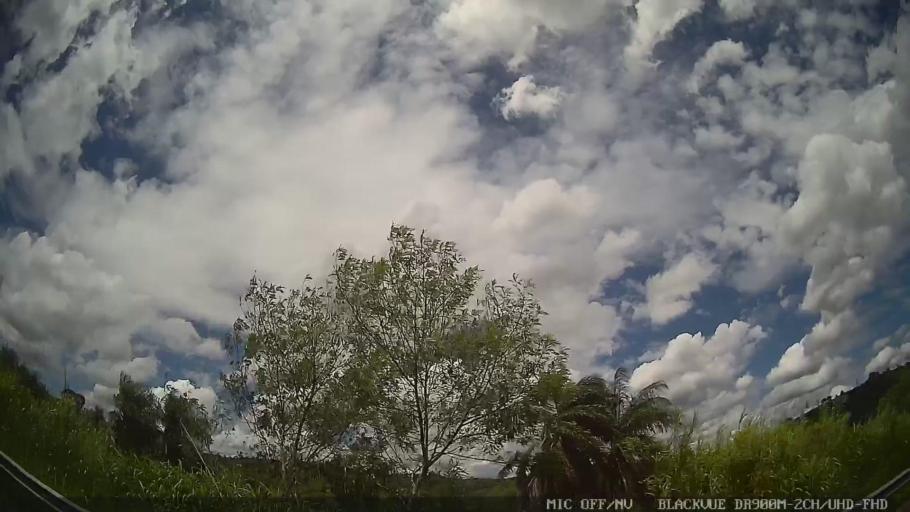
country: BR
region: Sao Paulo
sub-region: Pedreira
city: Pedreira
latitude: -22.7350
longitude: -46.9293
